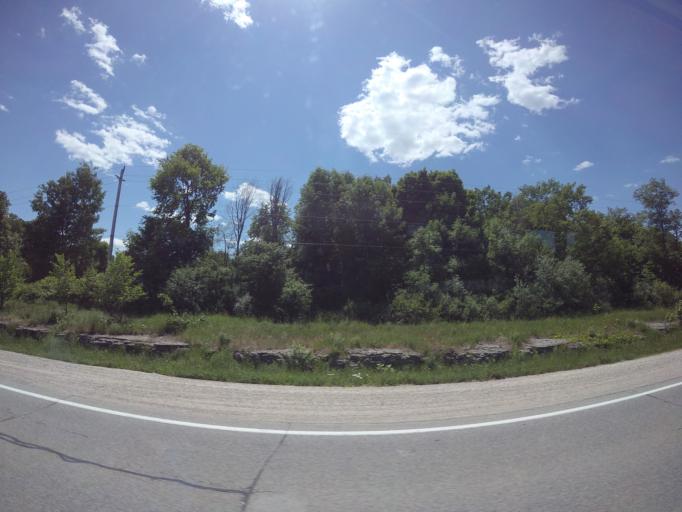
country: CA
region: Ontario
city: Carleton Place
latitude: 45.1288
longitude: -76.1680
